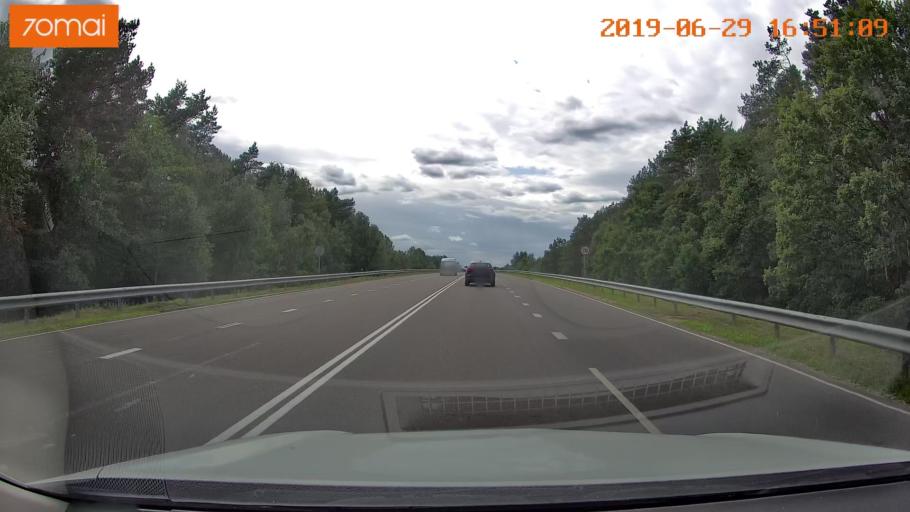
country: BY
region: Brest
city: Luninyets
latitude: 52.2801
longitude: 26.8295
